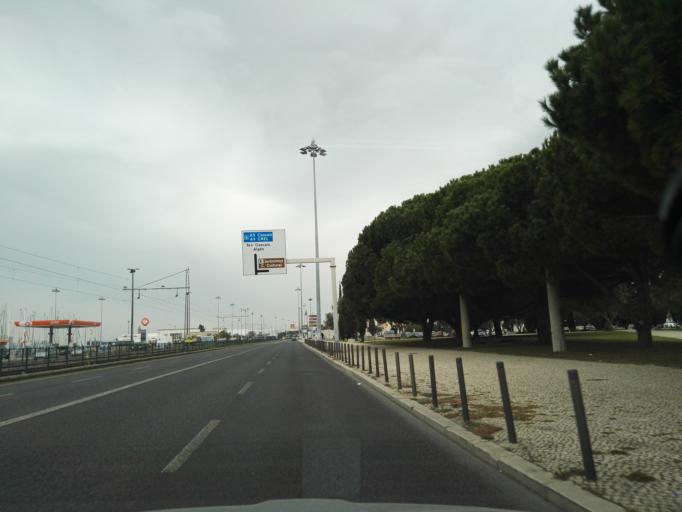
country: PT
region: Lisbon
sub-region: Oeiras
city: Alges
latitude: 38.6955
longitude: -9.2031
